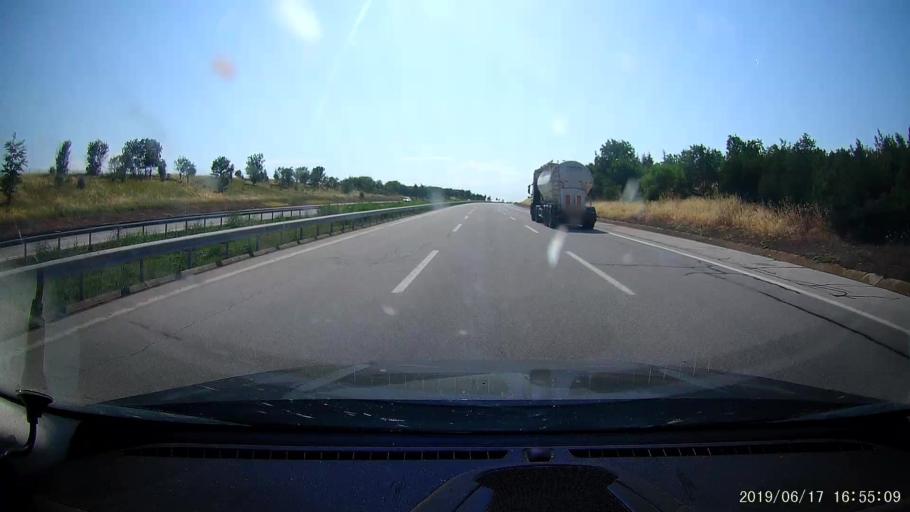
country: TR
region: Edirne
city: Haskoy
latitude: 41.5780
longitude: 26.9743
